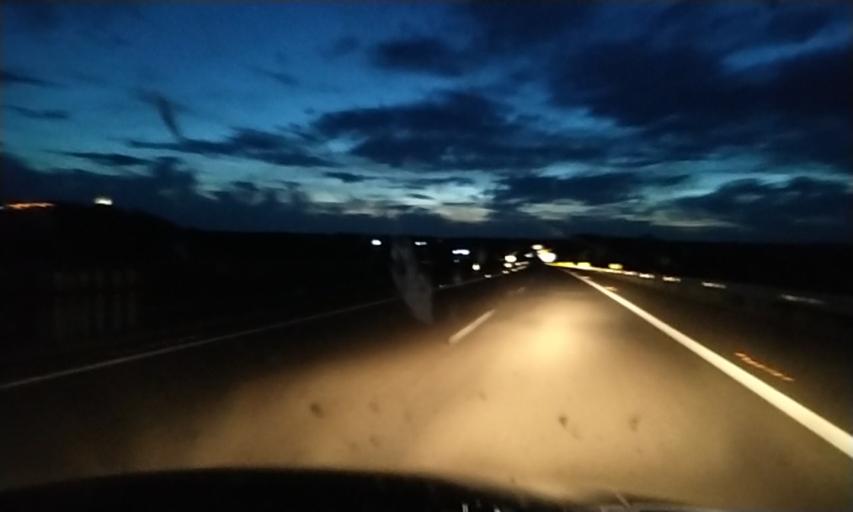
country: ES
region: Extremadura
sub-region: Provincia de Caceres
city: Galisteo
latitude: 39.9826
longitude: -6.2522
